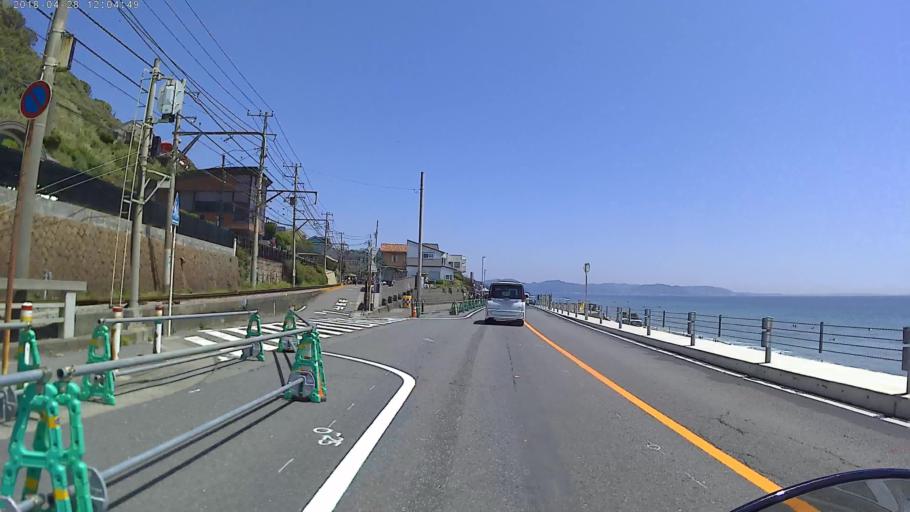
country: JP
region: Kanagawa
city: Kamakura
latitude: 35.3061
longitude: 139.5061
